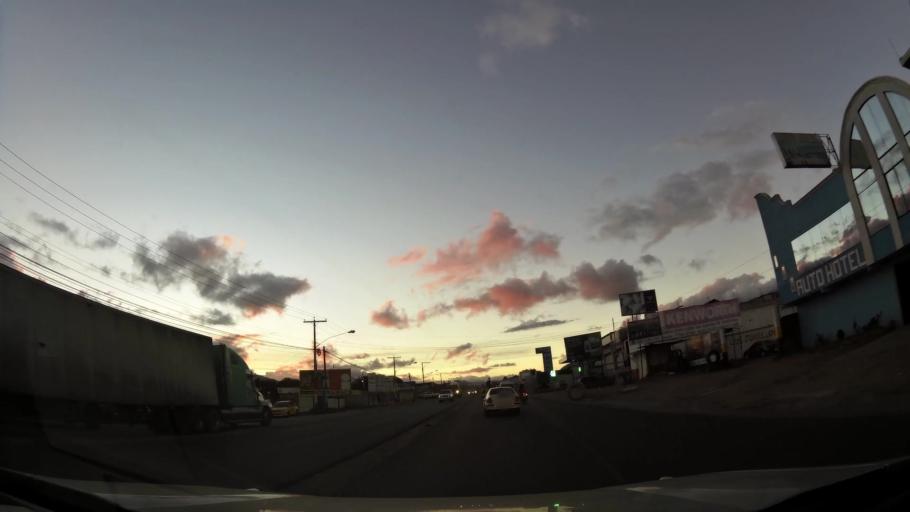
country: GT
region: Quetzaltenango
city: Olintepeque
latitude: 14.8618
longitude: -91.5274
